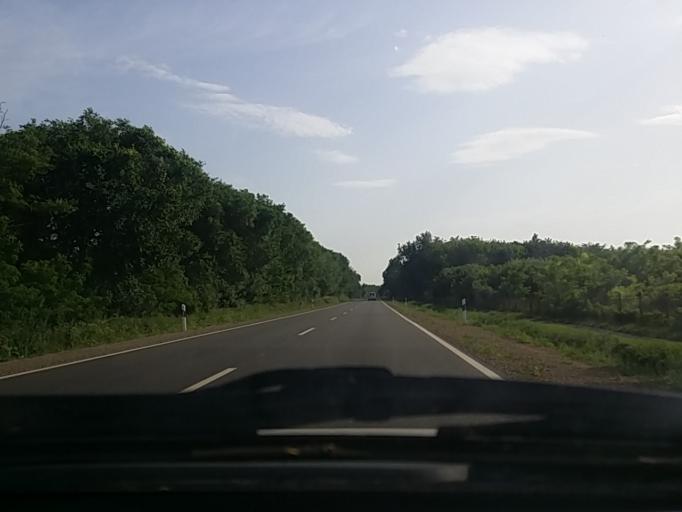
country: HU
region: Jasz-Nagykun-Szolnok
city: Jaszbereny
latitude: 47.4812
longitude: 19.8731
